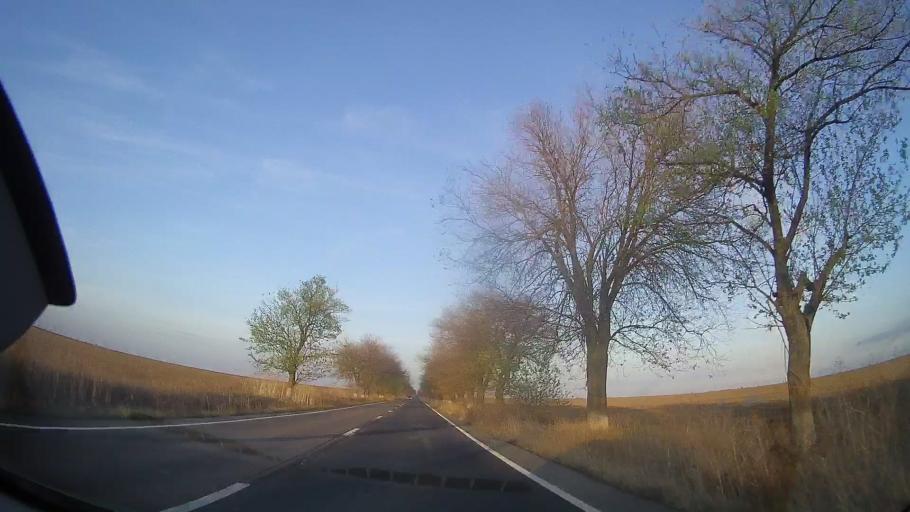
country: RO
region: Constanta
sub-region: Comuna Comana
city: Comana
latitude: 43.9041
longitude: 28.3296
